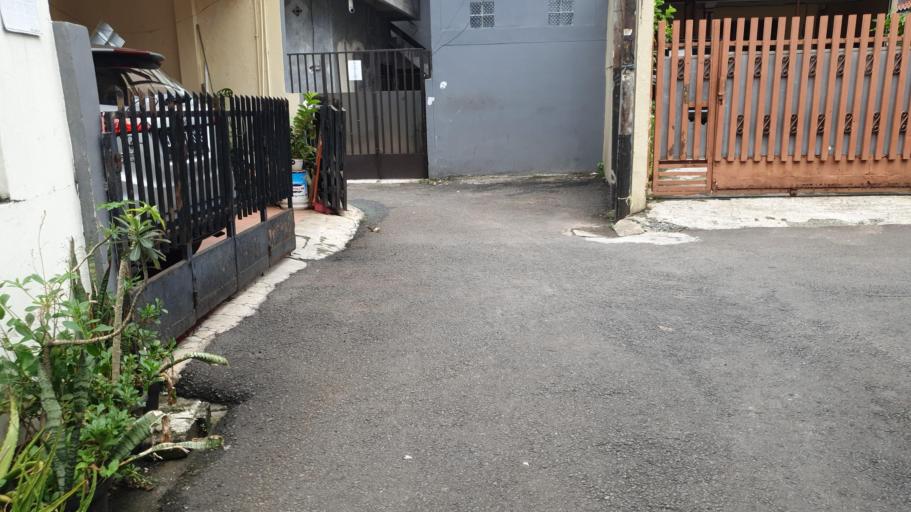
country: ID
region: Jakarta Raya
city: Jakarta
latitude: -6.2621
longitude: 106.7955
